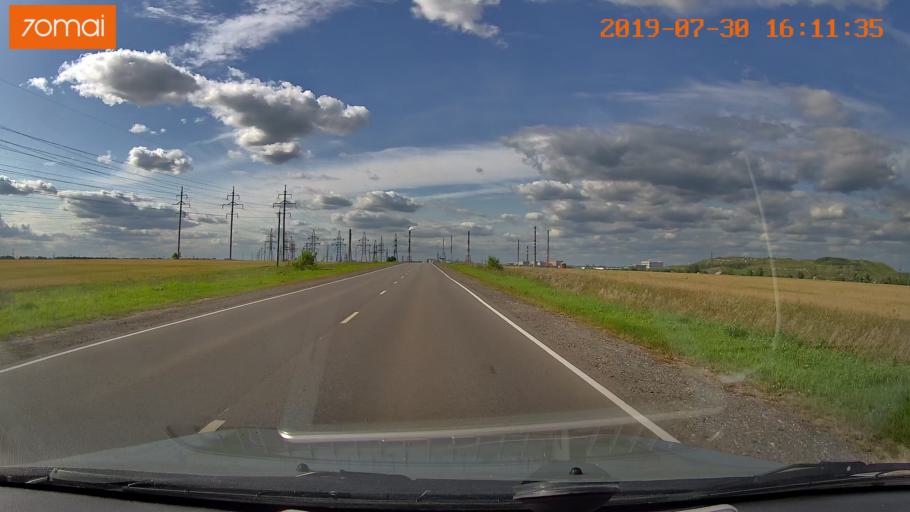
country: RU
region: Moskovskaya
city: Lopatinskiy
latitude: 55.2784
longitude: 38.7091
